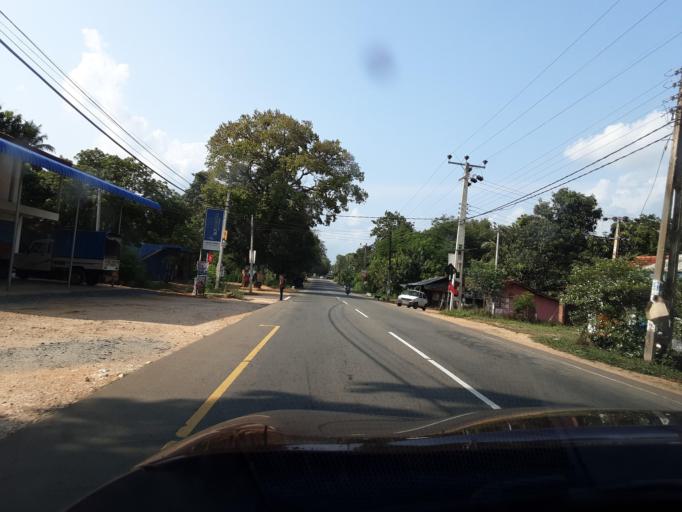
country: LK
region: Uva
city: Haputale
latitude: 6.5828
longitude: 81.1407
